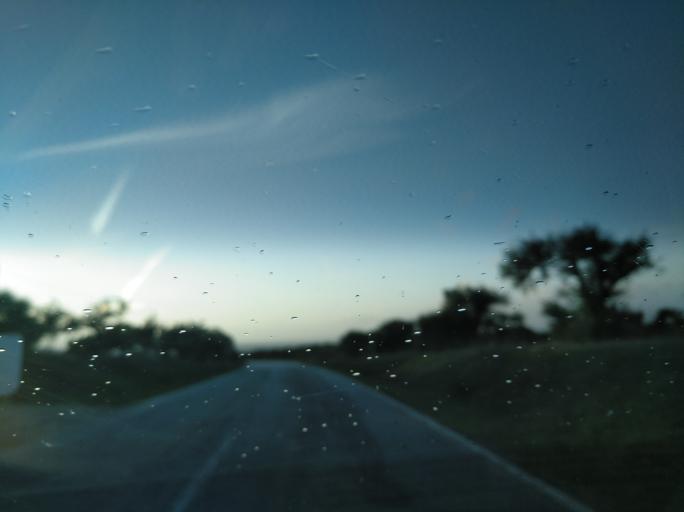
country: PT
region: Portalegre
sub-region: Campo Maior
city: Campo Maior
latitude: 39.0096
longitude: -7.1054
